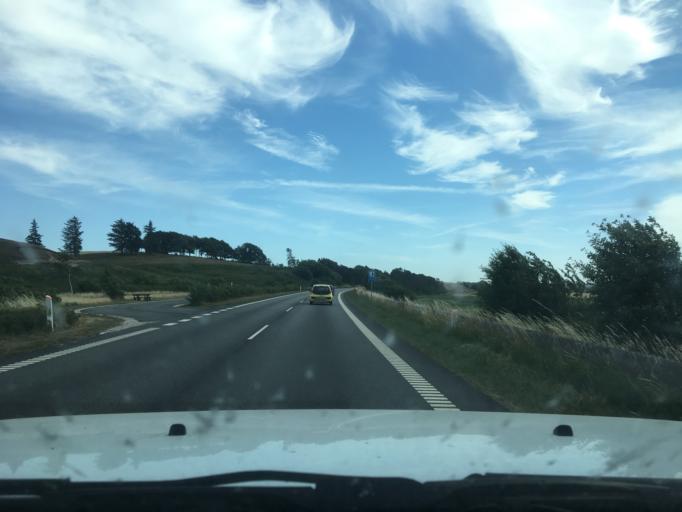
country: DK
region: Central Jutland
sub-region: Viborg Kommune
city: Viborg
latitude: 56.5675
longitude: 9.3846
